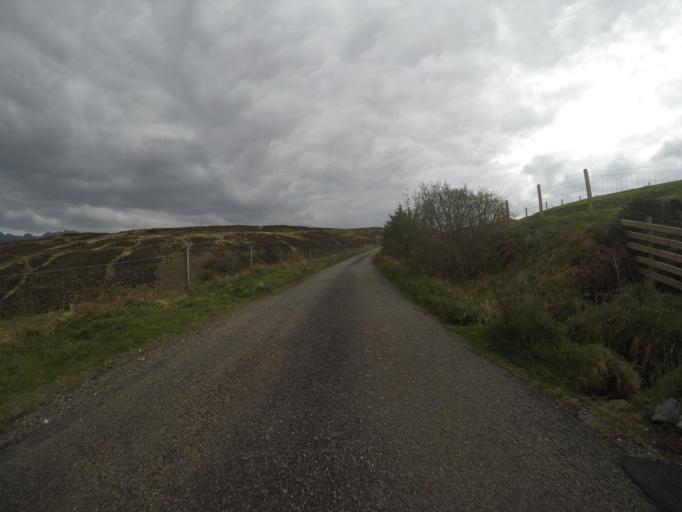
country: GB
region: Scotland
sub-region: Highland
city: Isle of Skye
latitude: 57.2973
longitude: -6.3580
